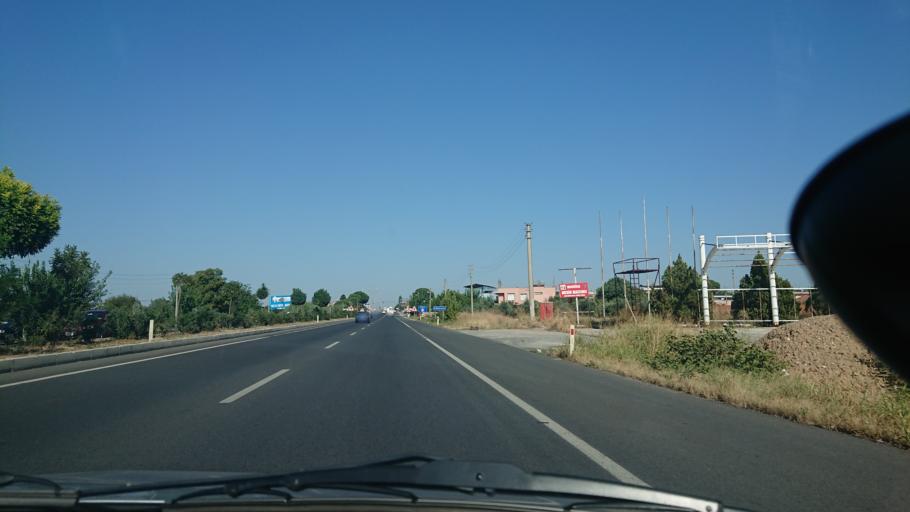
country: TR
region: Manisa
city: Ahmetli
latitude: 38.4990
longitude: 27.8665
